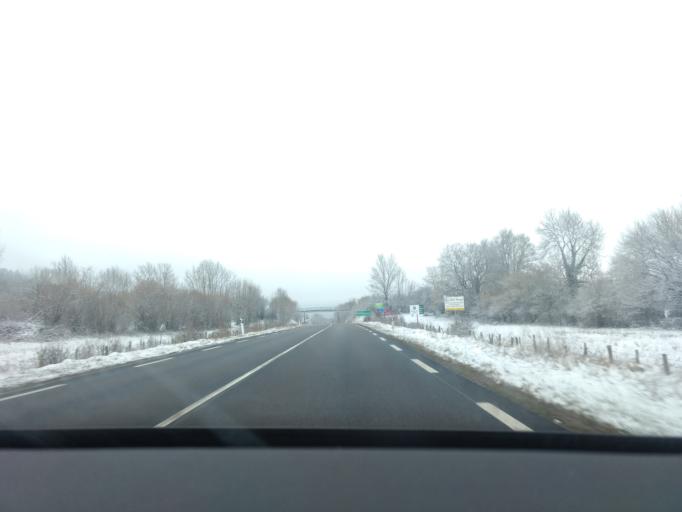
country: FR
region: Franche-Comte
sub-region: Departement du Jura
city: Champagnole
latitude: 46.7715
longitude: 5.9051
